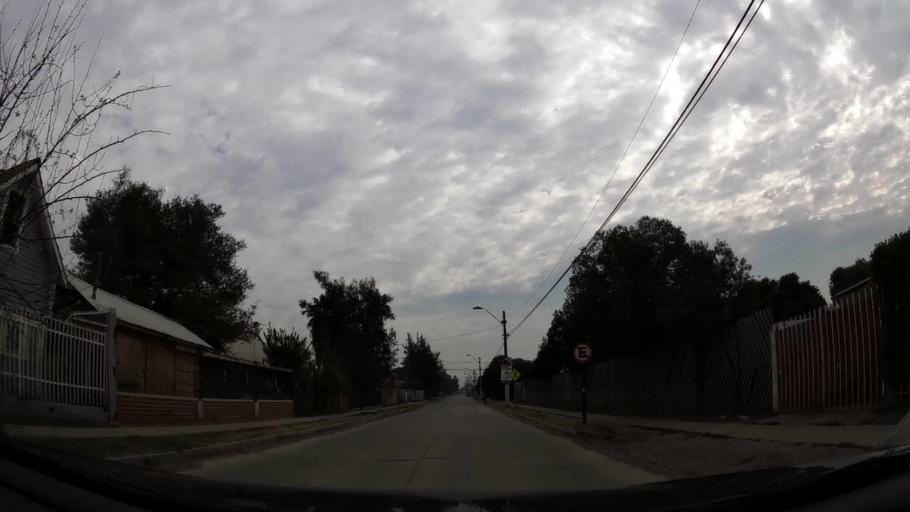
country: CL
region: Santiago Metropolitan
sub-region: Provincia de Chacabuco
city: Lampa
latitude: -33.2325
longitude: -70.8126
